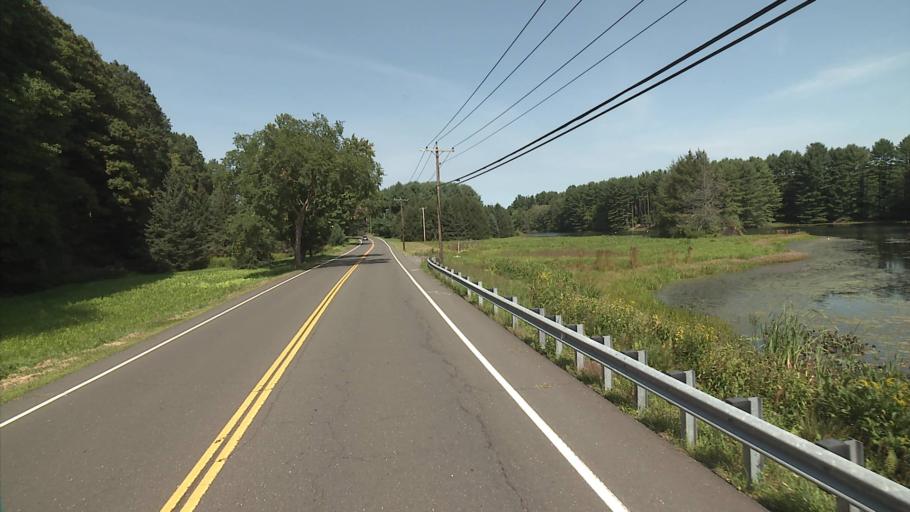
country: US
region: Connecticut
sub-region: Fairfield County
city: Westport
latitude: 41.2428
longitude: -73.3205
